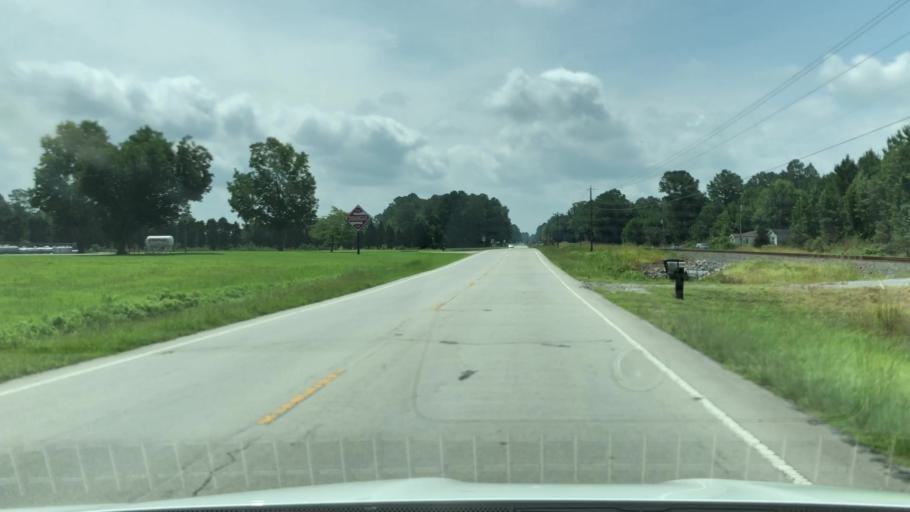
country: US
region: North Carolina
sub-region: Craven County
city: Vanceboro
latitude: 35.3438
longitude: -77.1510
